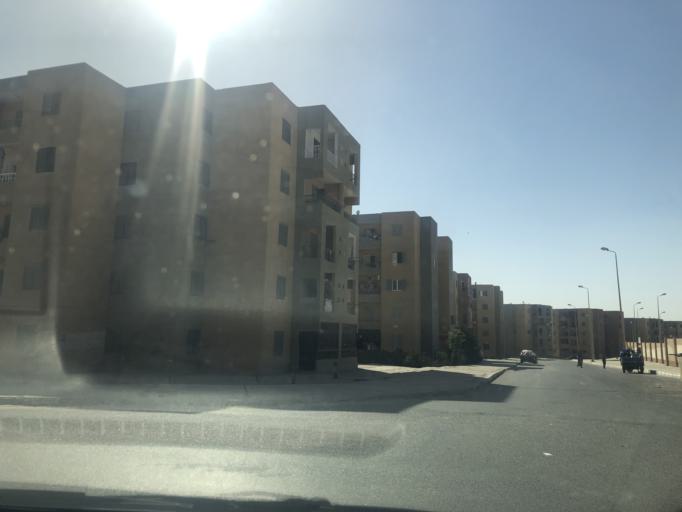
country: EG
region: Al Jizah
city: Madinat Sittah Uktubar
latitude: 29.9241
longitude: 30.9347
